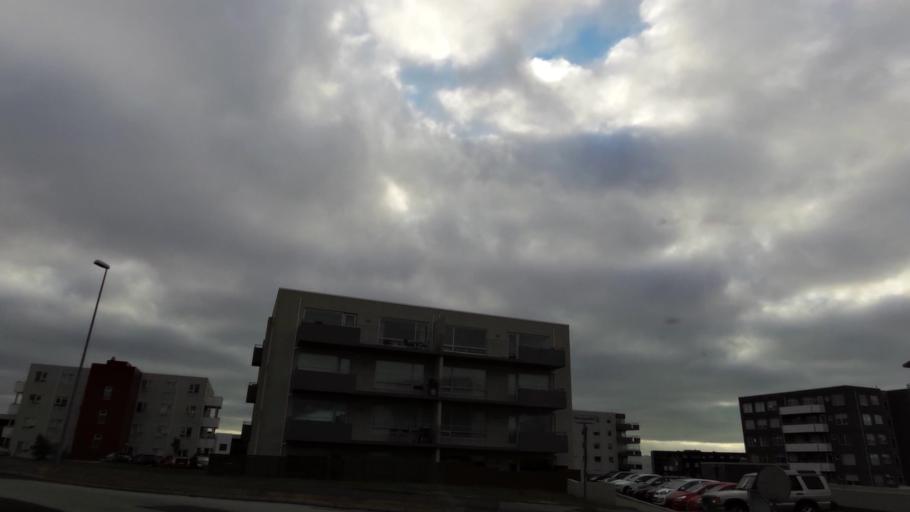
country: IS
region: Capital Region
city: Hafnarfjoerdur
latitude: 64.0495
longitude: -21.9814
